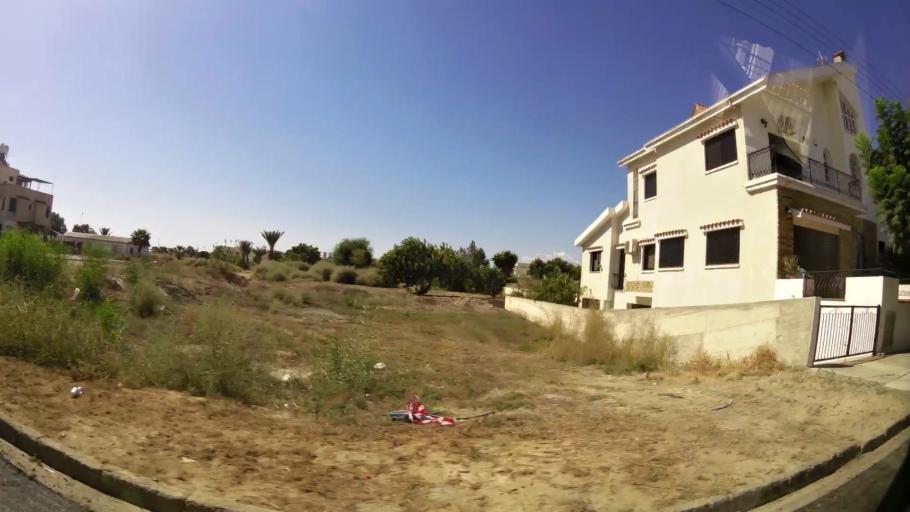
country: CY
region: Larnaka
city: Voroklini
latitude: 34.9588
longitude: 33.6544
